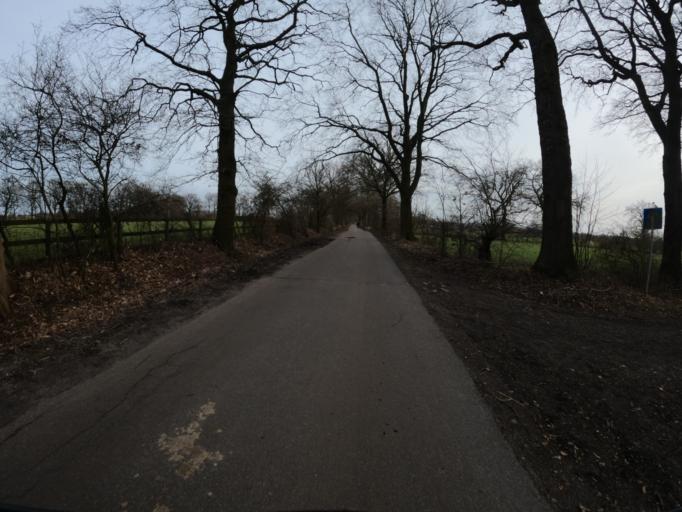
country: DE
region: Schleswig-Holstein
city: Rellingen
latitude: 53.6038
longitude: 9.7897
